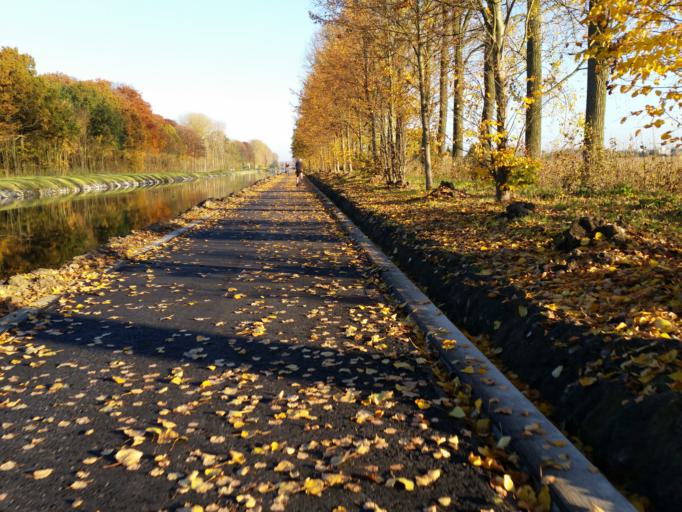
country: BE
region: Flanders
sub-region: Provincie Vlaams-Brabant
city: Haacht
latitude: 50.9522
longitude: 4.6156
